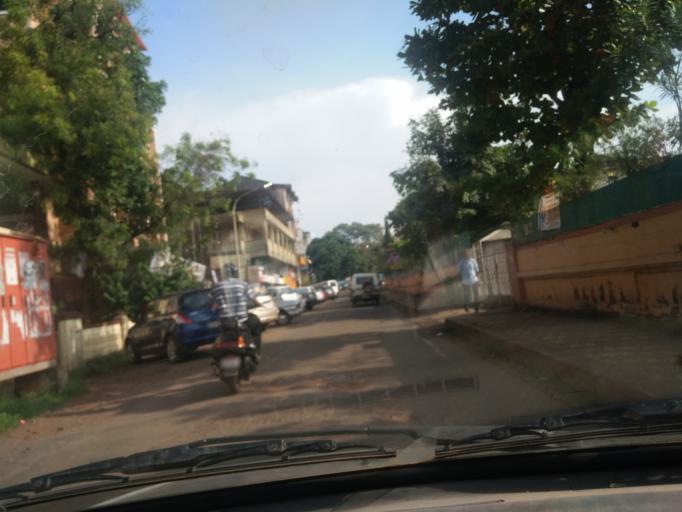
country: IN
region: Goa
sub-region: South Goa
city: Madgaon
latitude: 15.2729
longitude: 73.9566
